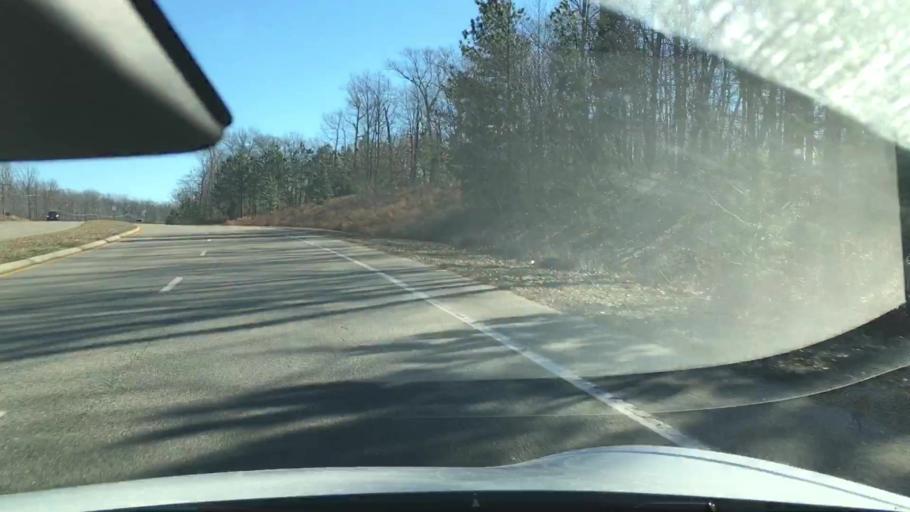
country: US
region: Virginia
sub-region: Chesterfield County
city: Bon Air
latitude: 37.5424
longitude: -77.6491
